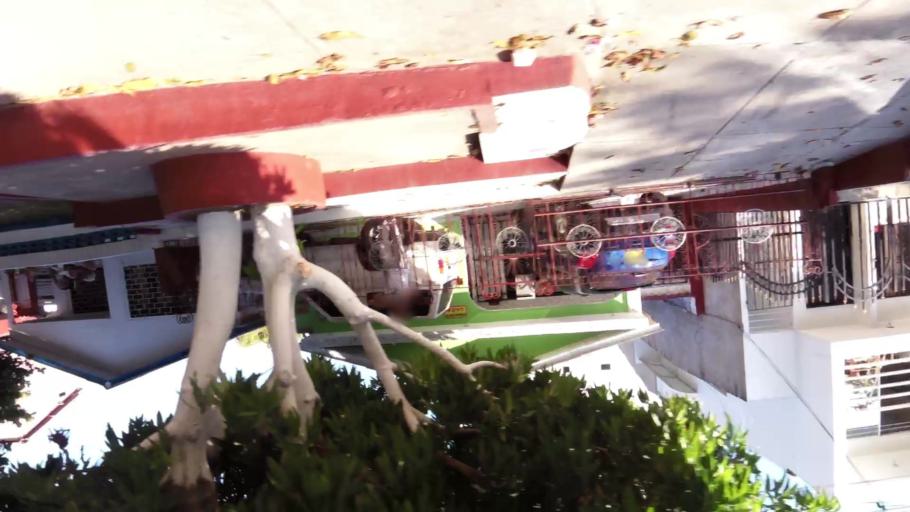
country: CO
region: Bolivar
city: Cartagena
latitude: 10.3837
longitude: -75.4851
